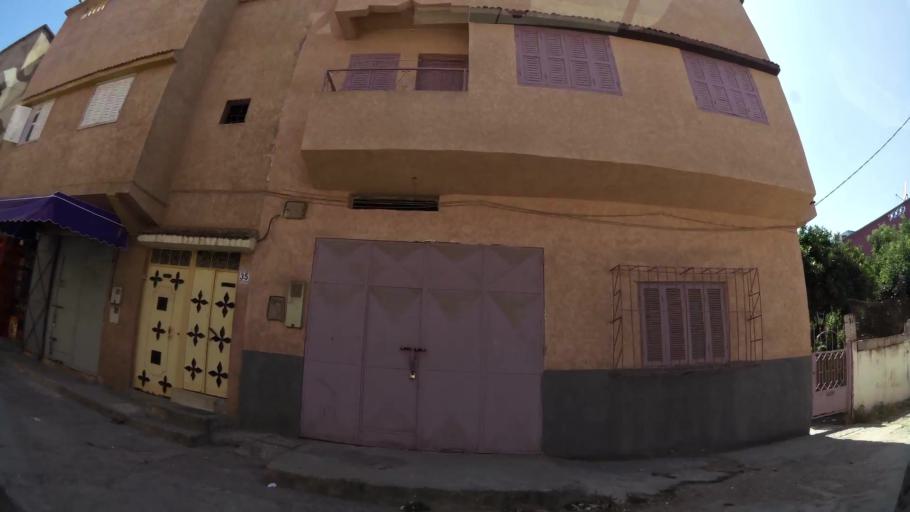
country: MA
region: Gharb-Chrarda-Beni Hssen
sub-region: Kenitra Province
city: Kenitra
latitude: 34.2431
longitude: -6.5546
